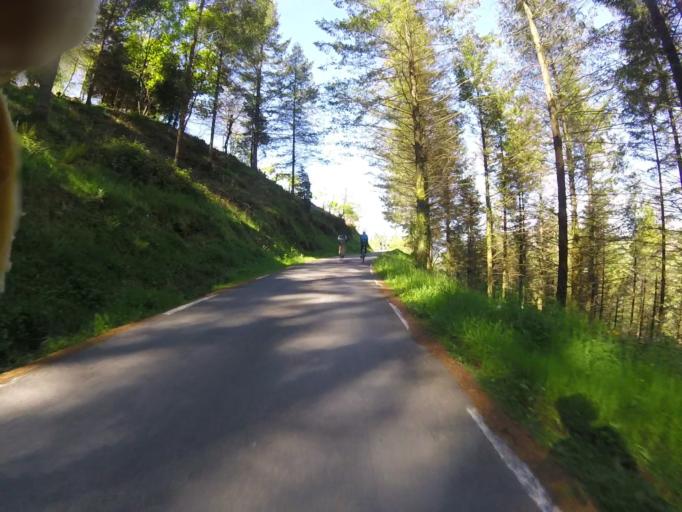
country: ES
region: Basque Country
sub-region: Provincia de Guipuzcoa
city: Errezil
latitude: 43.1904
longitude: -2.2043
